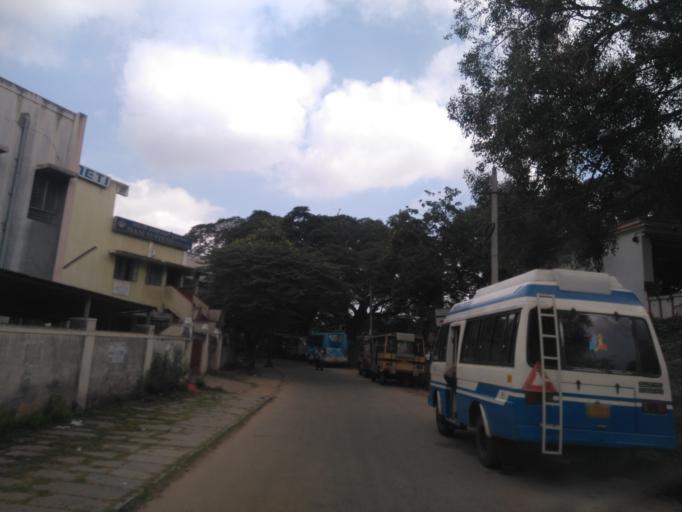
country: IN
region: Karnataka
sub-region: Mysore
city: Mysore
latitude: 12.3005
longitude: 76.6565
